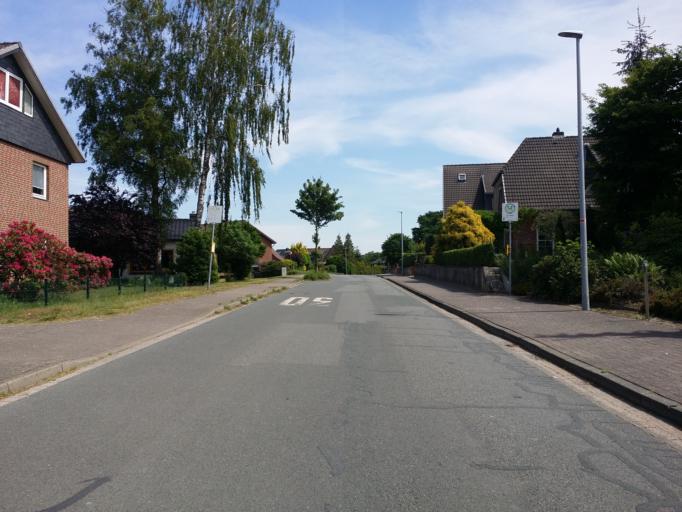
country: DE
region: Lower Saxony
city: Syke
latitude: 52.9429
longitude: 8.8352
